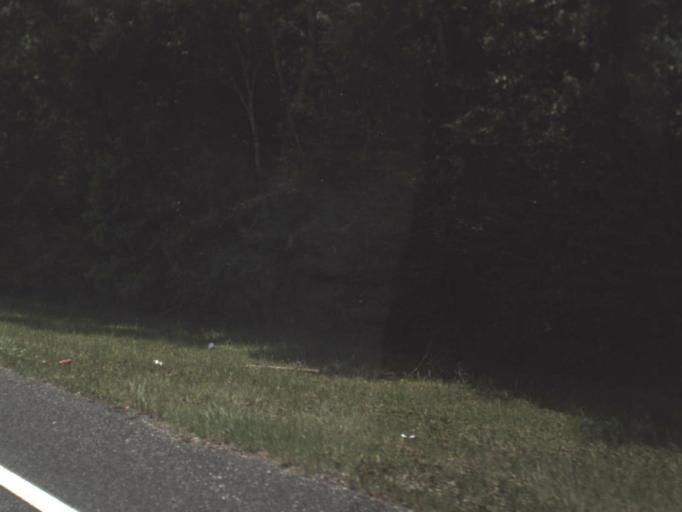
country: US
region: Florida
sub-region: Dixie County
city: Cross City
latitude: 29.6694
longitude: -83.2250
